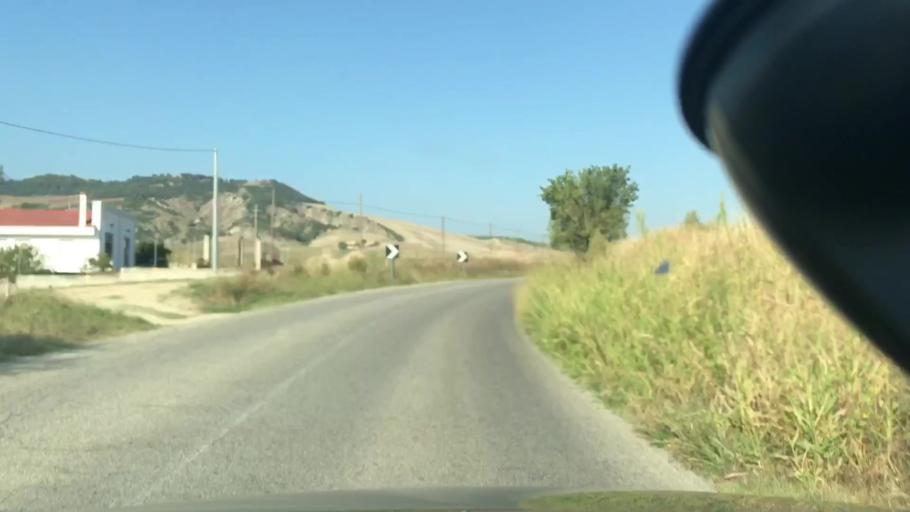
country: IT
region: Basilicate
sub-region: Provincia di Matera
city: La Martella
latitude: 40.6585
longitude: 16.5174
